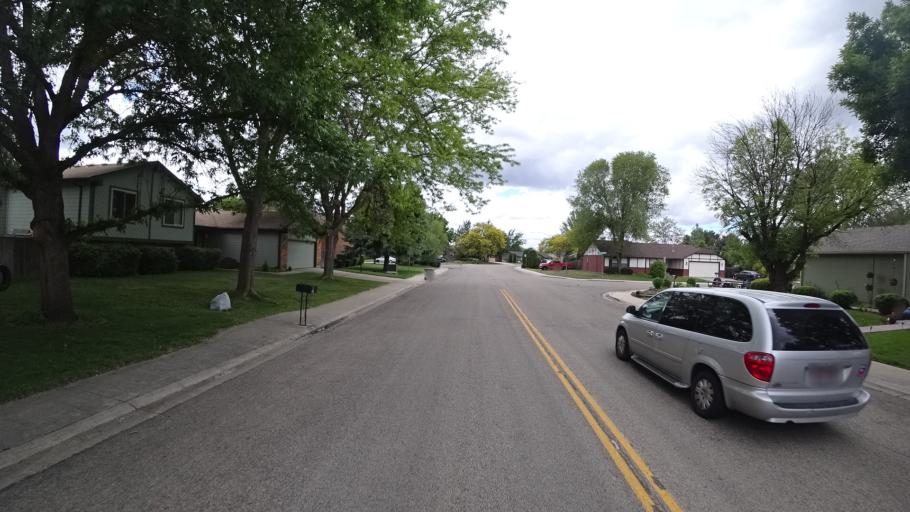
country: US
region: Idaho
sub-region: Ada County
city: Garden City
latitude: 43.6603
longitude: -116.2572
